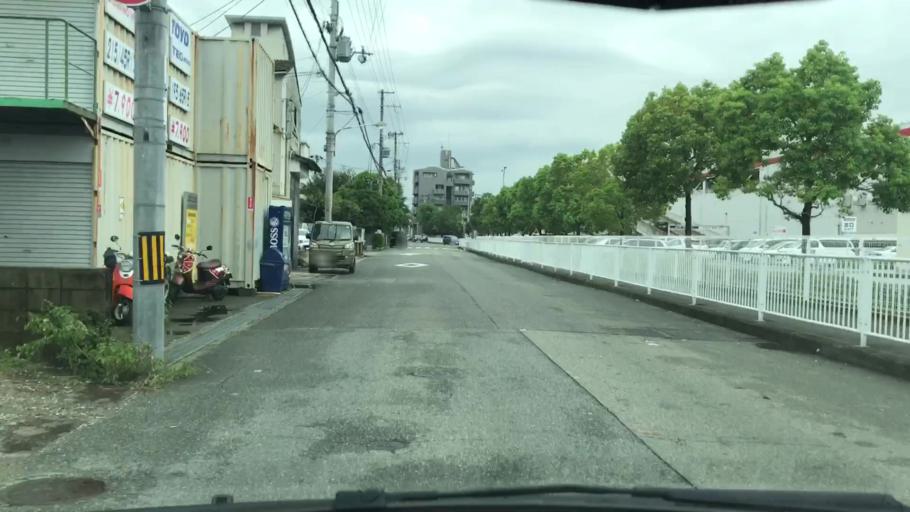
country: JP
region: Hyogo
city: Amagasaki
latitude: 34.7431
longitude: 135.4449
